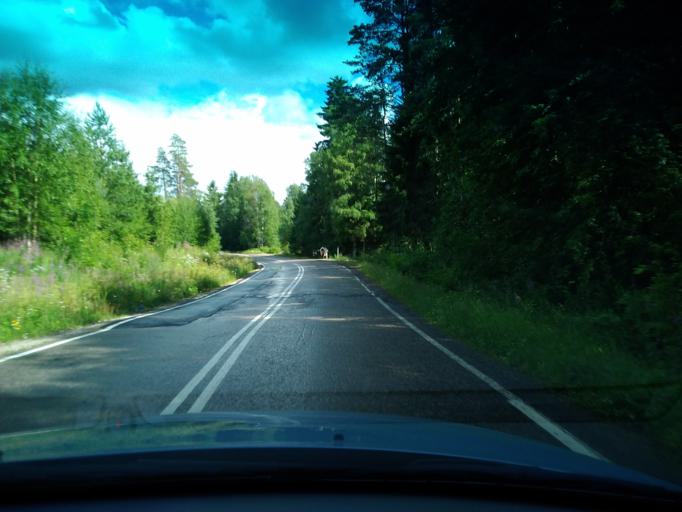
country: FI
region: Central Finland
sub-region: Saarijaervi-Viitasaari
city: Saarijaervi
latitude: 62.7351
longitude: 25.1305
